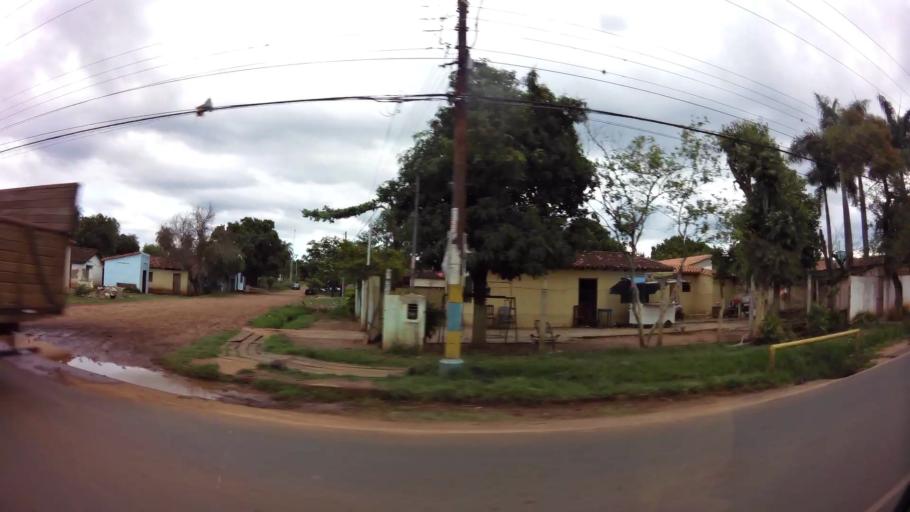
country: PY
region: Central
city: San Lorenzo
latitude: -25.2894
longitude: -57.4846
